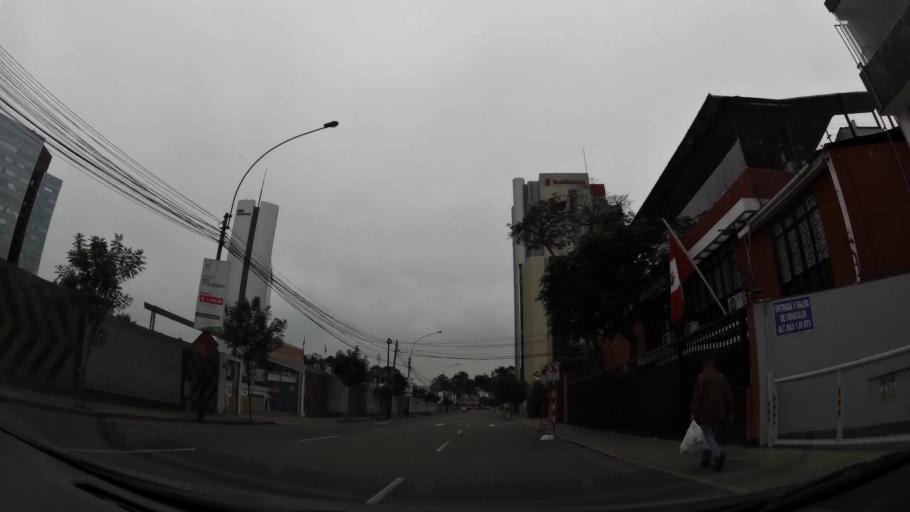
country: PE
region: Lima
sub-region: Lima
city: San Luis
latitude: -12.0949
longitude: -77.0235
